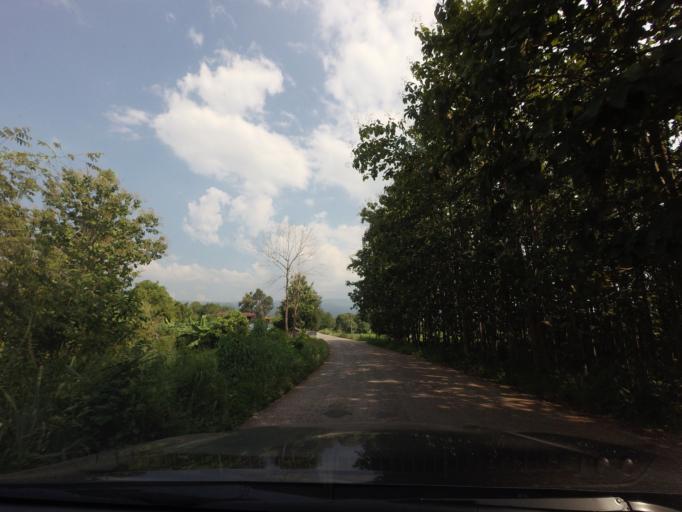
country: TH
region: Phitsanulok
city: Nakhon Thai
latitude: 17.0539
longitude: 100.9018
